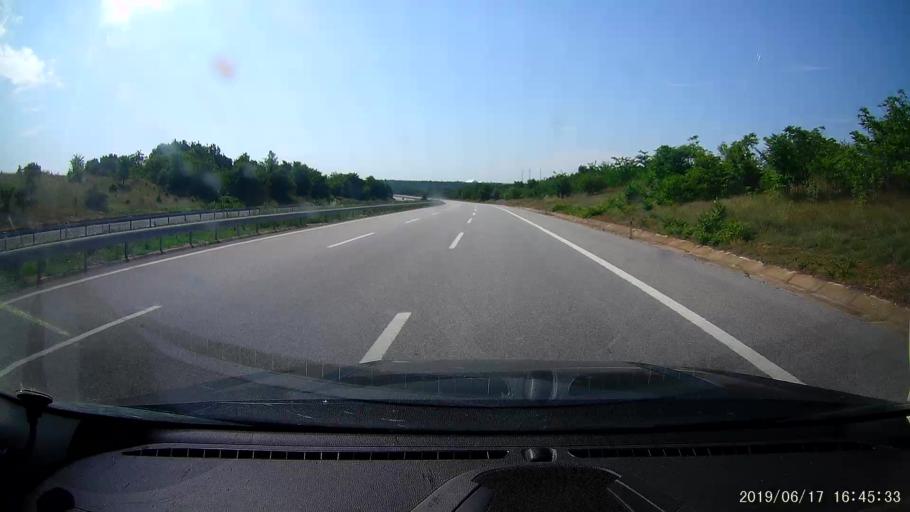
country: TR
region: Kirklareli
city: Babaeski
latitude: 41.4900
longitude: 27.2298
